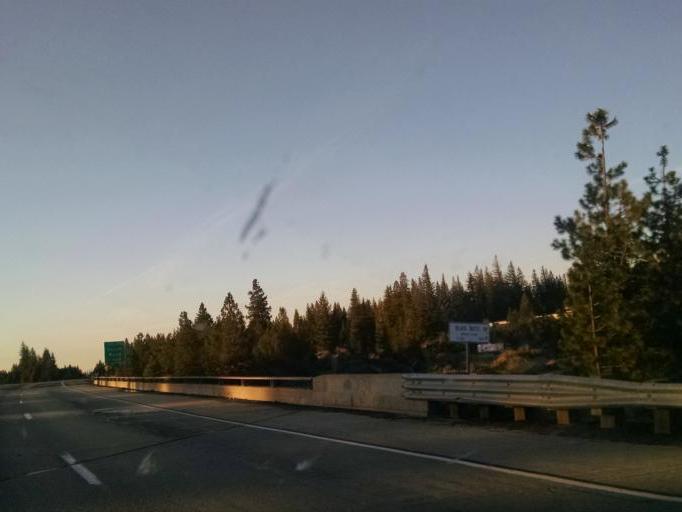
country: US
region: California
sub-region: Siskiyou County
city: Weed
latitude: 41.3759
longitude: -122.3752
